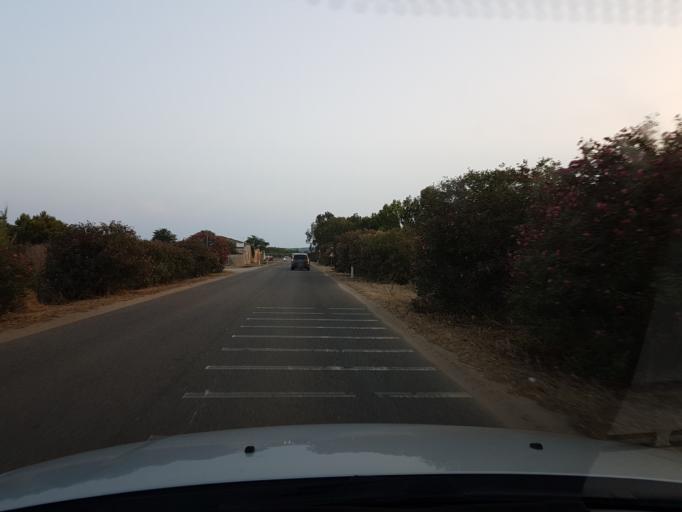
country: IT
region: Sardinia
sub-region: Provincia di Oristano
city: Cabras
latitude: 39.9227
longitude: 8.4523
